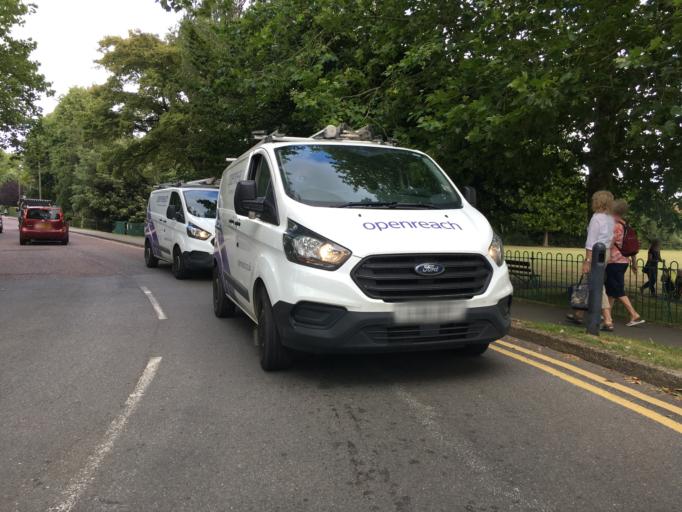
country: GB
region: England
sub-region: Kent
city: Tenterden
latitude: 51.0696
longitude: 0.6902
